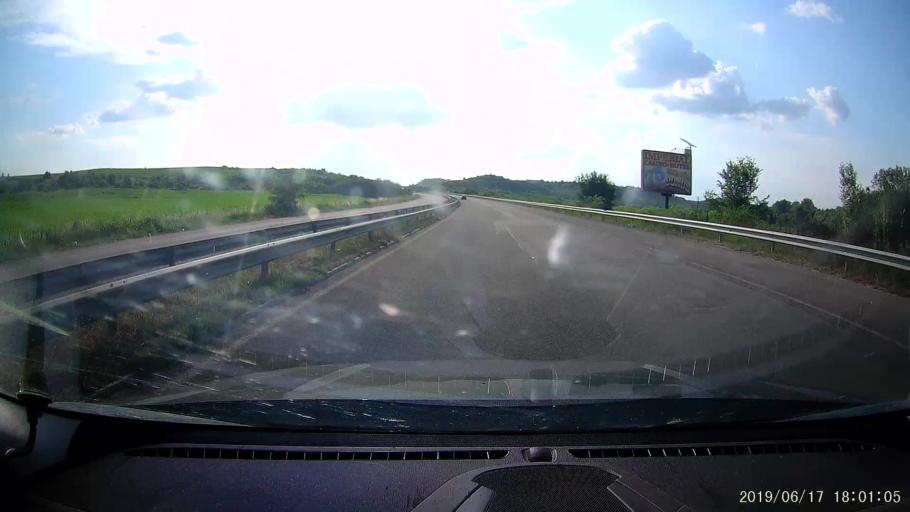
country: BG
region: Khaskovo
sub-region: Obshtina Svilengrad
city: Svilengrad
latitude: 41.7437
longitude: 26.2647
